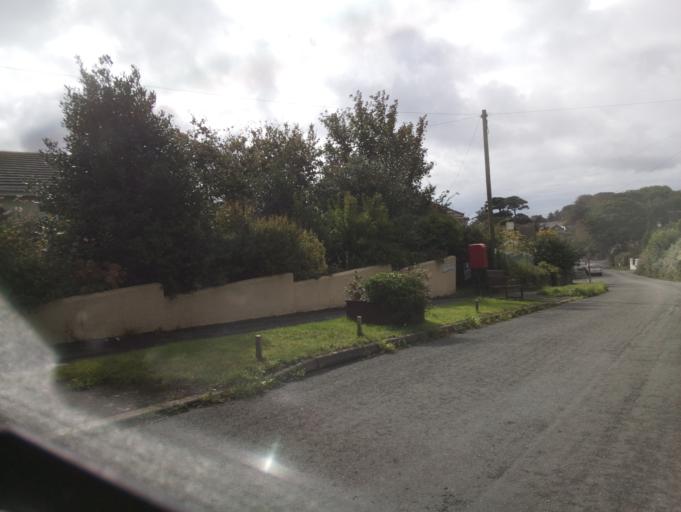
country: GB
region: England
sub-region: Devon
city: Dartmouth
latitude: 50.3287
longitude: -3.6005
